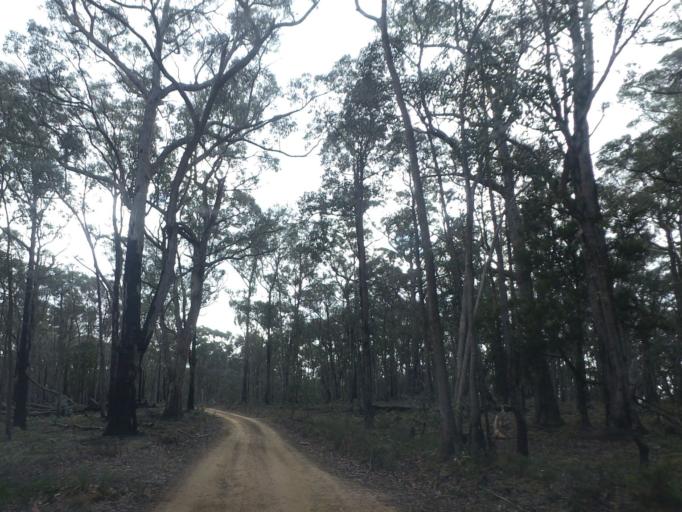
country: AU
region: Victoria
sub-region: Moorabool
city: Bacchus Marsh
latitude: -37.4542
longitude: 144.3248
